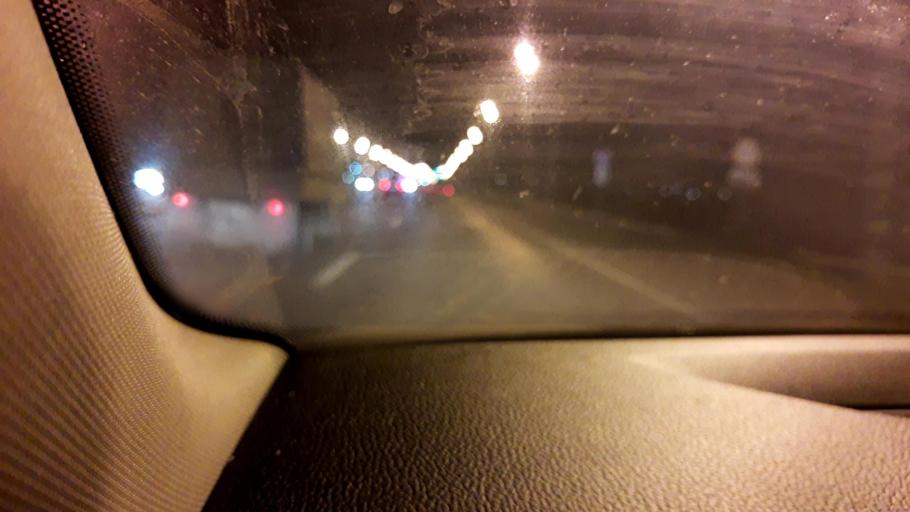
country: RU
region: Moskovskaya
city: Solnechnogorsk
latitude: 56.2284
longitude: 36.9119
